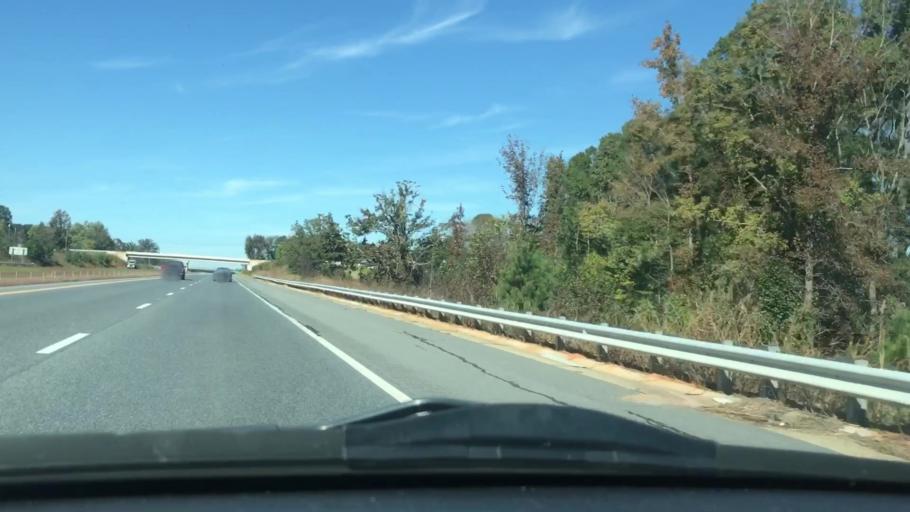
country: US
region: North Carolina
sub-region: Randolph County
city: Randleman
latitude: 35.8290
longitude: -79.8573
